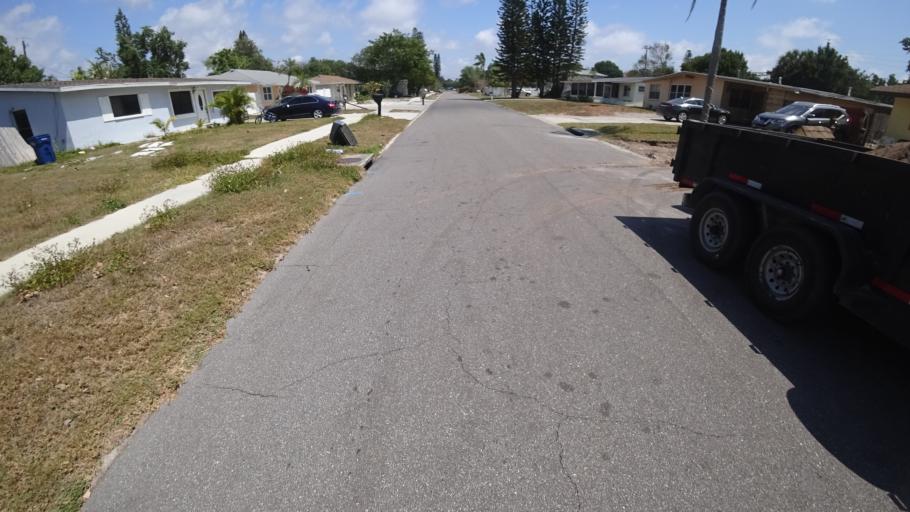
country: US
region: Florida
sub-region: Manatee County
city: Bayshore Gardens
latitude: 27.4298
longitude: -82.5811
